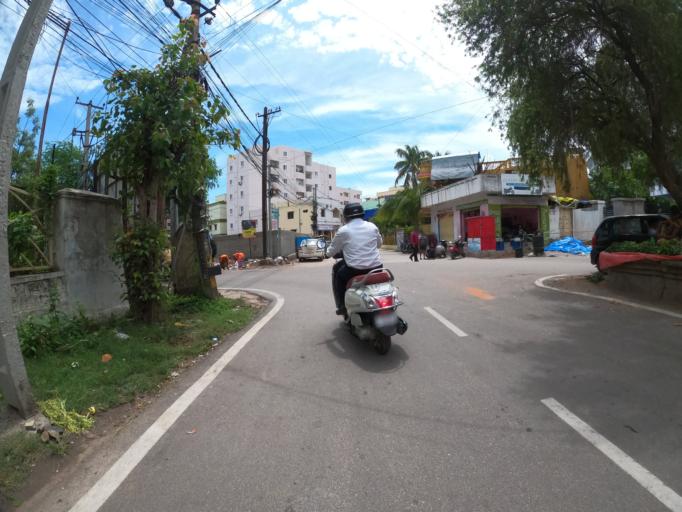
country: IN
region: Telangana
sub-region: Hyderabad
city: Hyderabad
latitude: 17.3664
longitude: 78.4223
